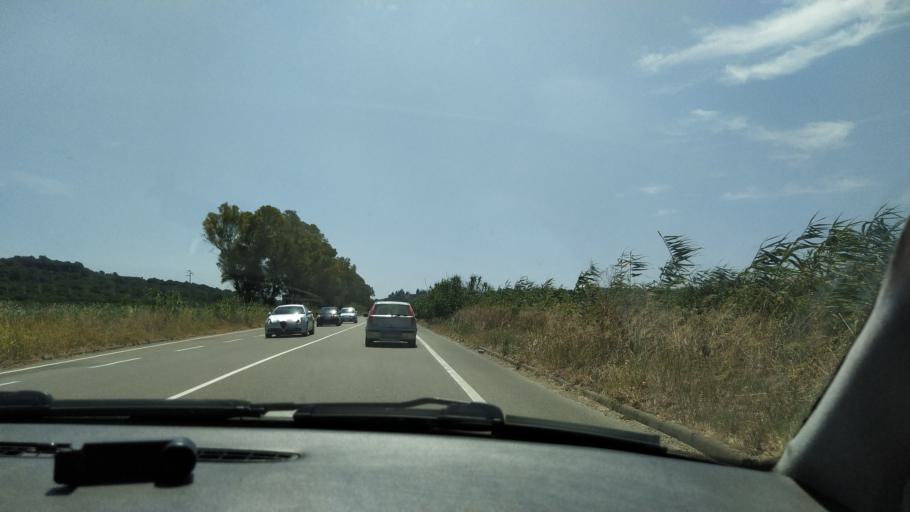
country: IT
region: Apulia
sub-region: Provincia di Taranto
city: Marina di Ginosa
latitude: 40.4391
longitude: 16.7850
